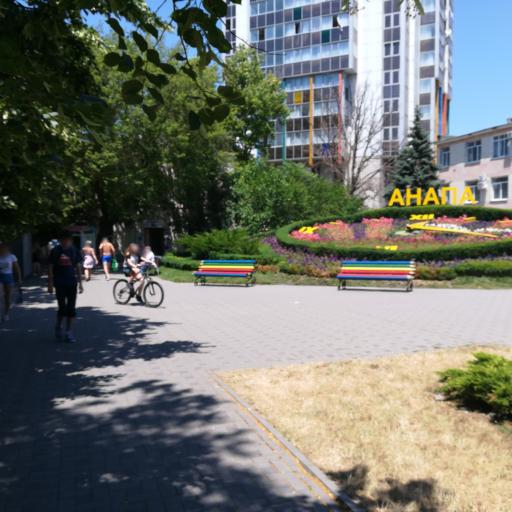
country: RU
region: Krasnodarskiy
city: Anapa
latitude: 44.8934
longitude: 37.3091
